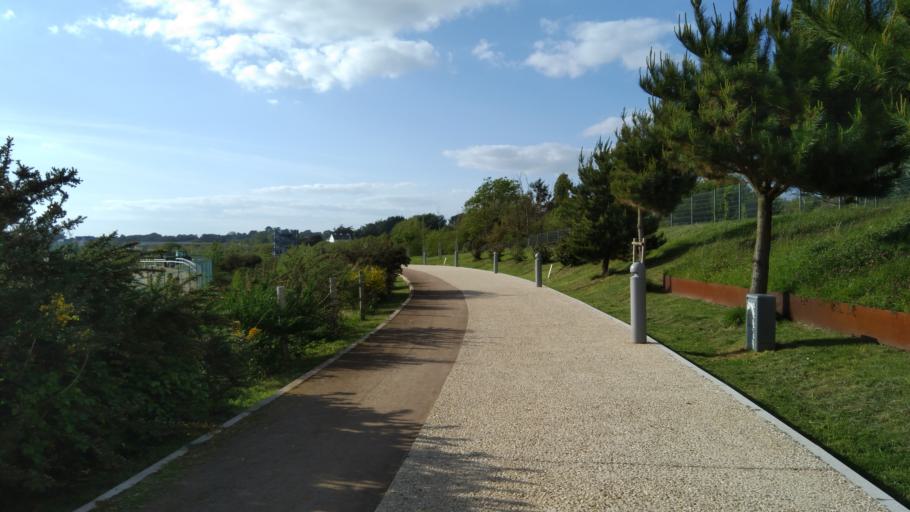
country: FR
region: Pays de la Loire
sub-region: Departement de la Loire-Atlantique
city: Pornichet
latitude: 47.2616
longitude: -2.3265
